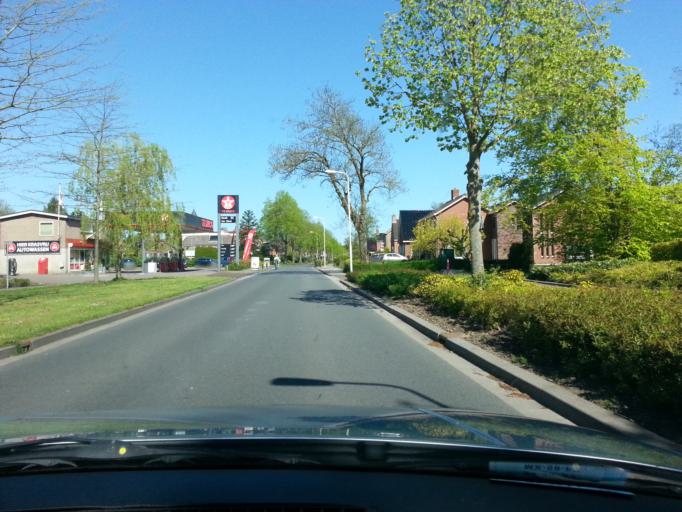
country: NL
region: Friesland
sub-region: Gemeente Achtkarspelen
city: Buitenpost
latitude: 53.2491
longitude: 6.1494
